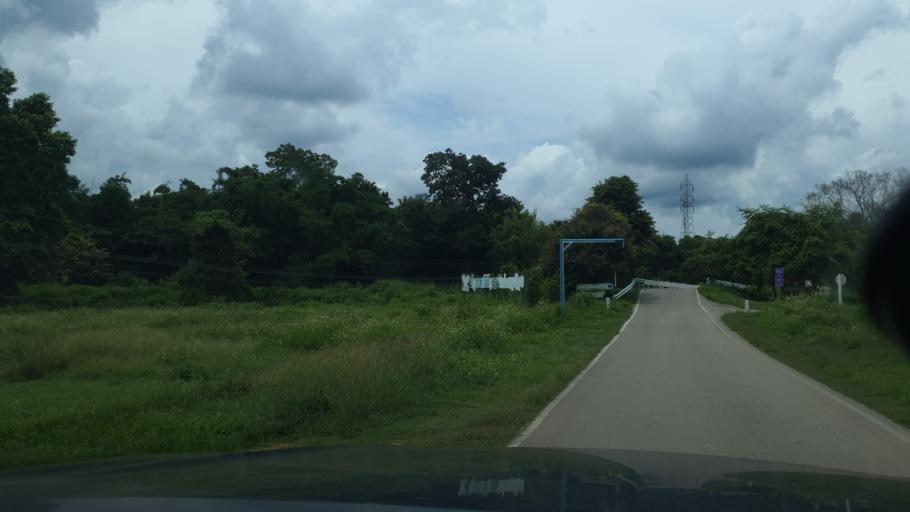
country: TH
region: Lampang
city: Hang Chat
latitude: 18.4057
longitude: 99.2615
